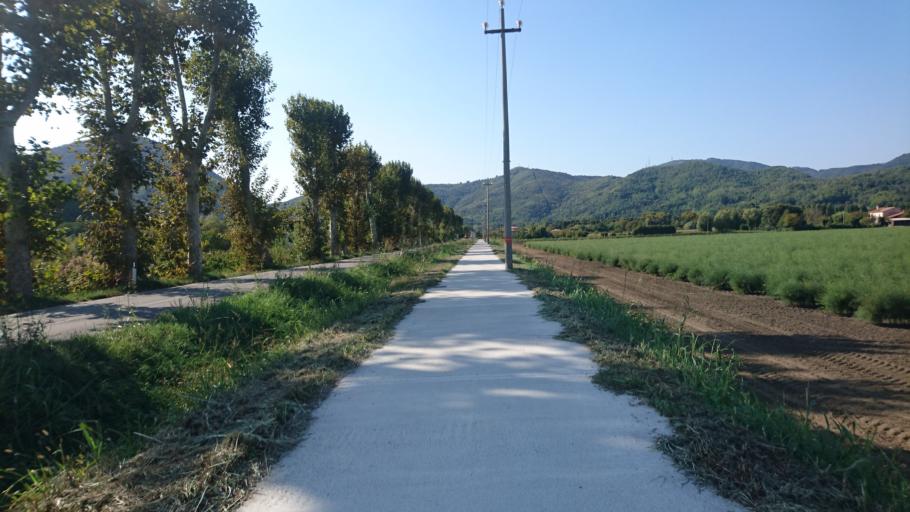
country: IT
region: Veneto
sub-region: Provincia di Padova
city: Galzignano
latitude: 45.2878
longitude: 11.7476
